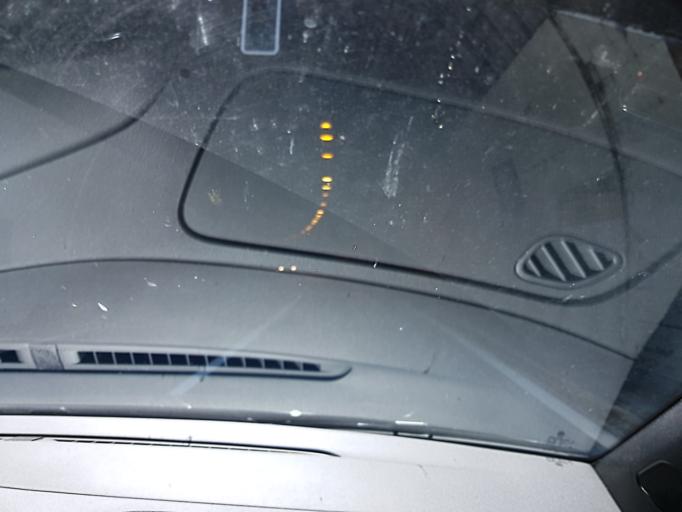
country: CH
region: Grisons
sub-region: Albula District
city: Tiefencastel
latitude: 46.6773
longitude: 9.5432
